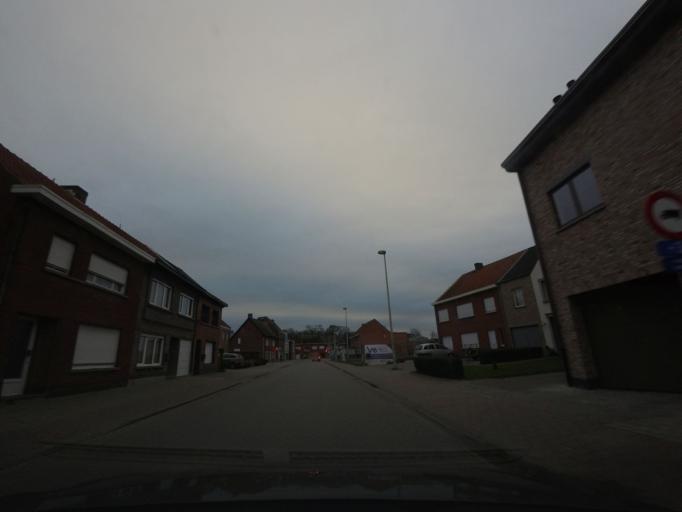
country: BE
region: Flanders
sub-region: Provincie Antwerpen
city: Brecht
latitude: 51.3525
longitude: 4.6407
